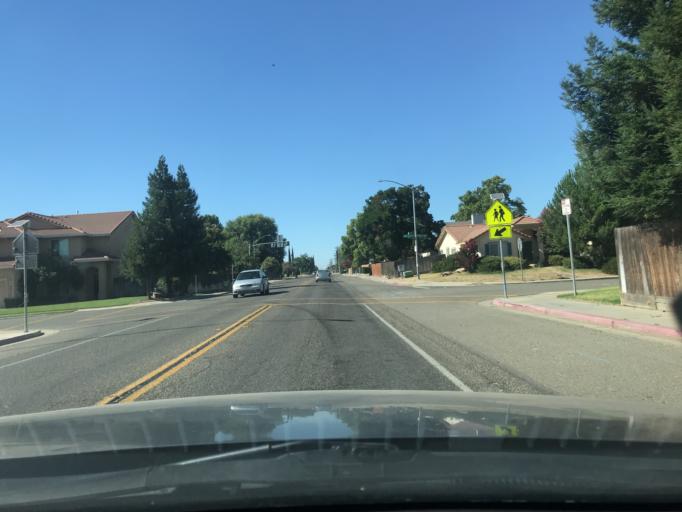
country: US
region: California
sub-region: Merced County
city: Merced
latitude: 37.3282
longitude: -120.5409
